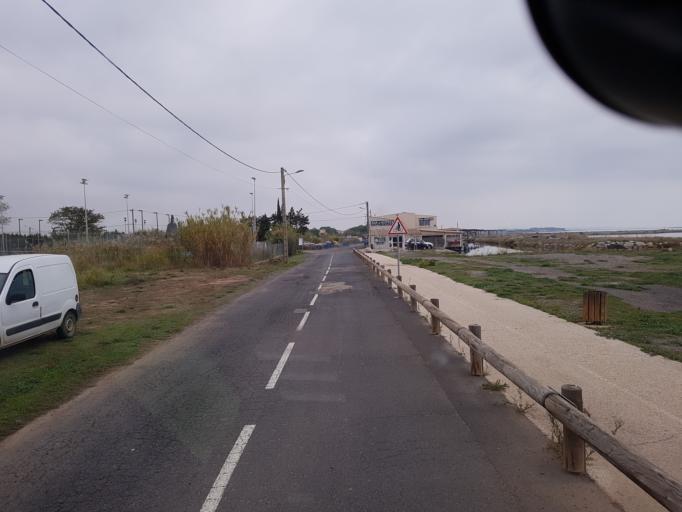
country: FR
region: Languedoc-Roussillon
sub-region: Departement de l'Herault
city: Marseillan
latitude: 43.3609
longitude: 3.5356
